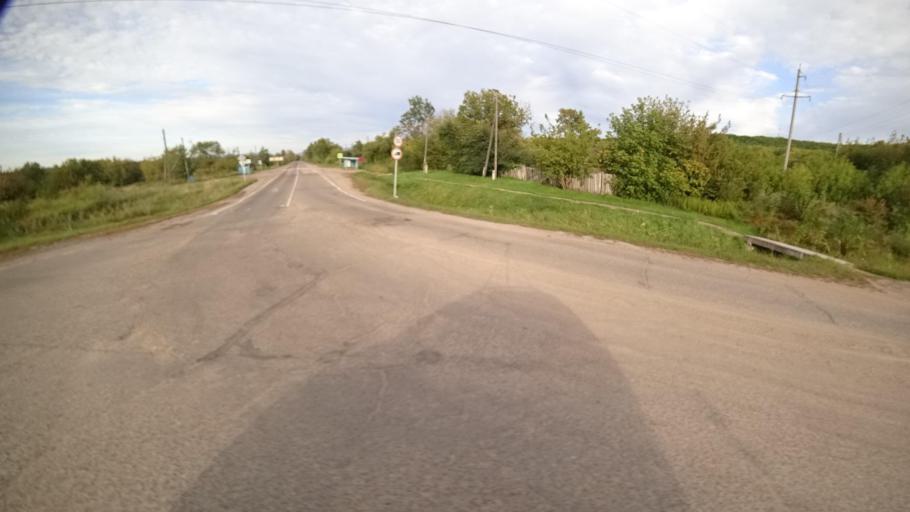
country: RU
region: Primorskiy
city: Yakovlevka
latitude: 44.4177
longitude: 133.4524
